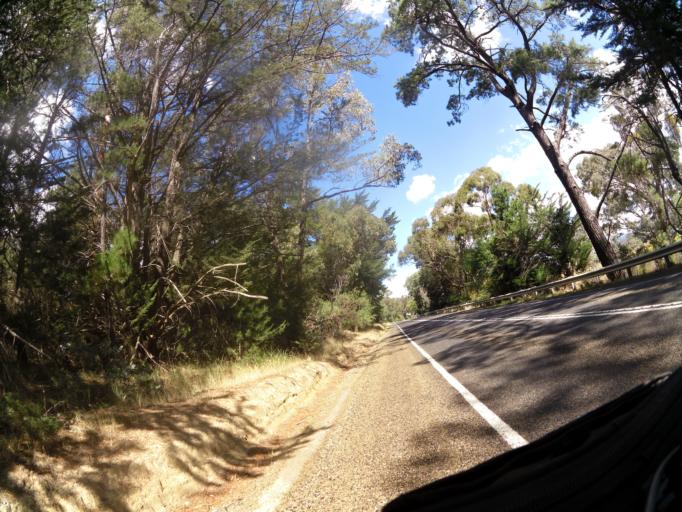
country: AU
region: Victoria
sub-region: Mansfield
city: Mansfield
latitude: -36.8279
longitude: 146.0083
